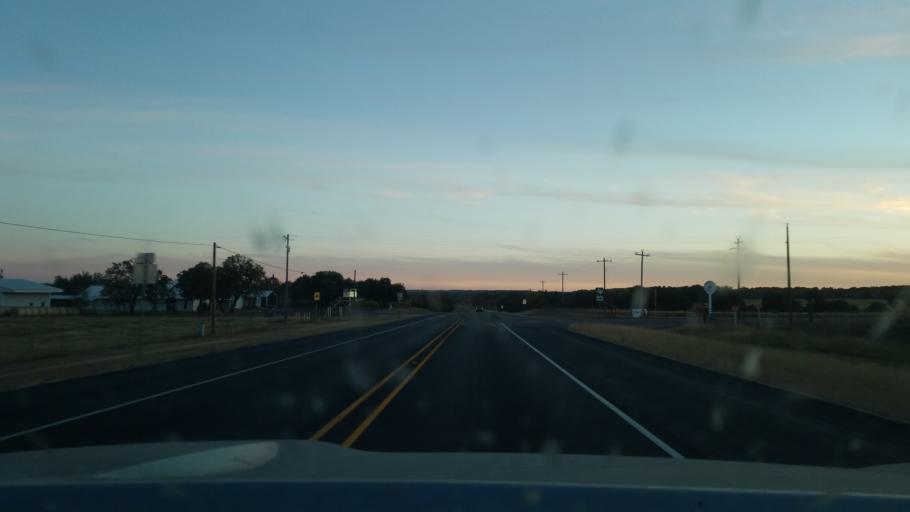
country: US
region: Texas
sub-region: Stephens County
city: Breckenridge
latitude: 32.6024
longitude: -98.8998
